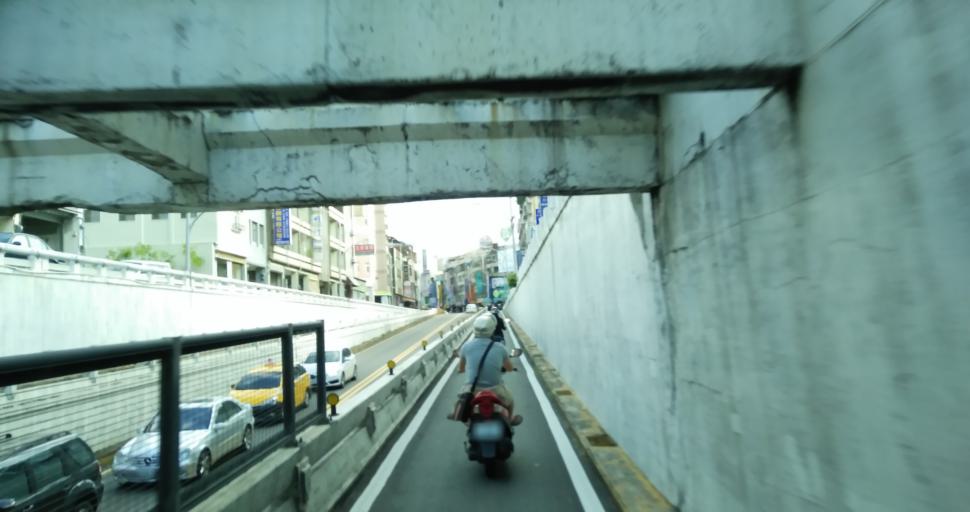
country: TW
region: Taiwan
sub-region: Hsinchu
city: Hsinchu
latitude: 24.7986
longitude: 120.9680
